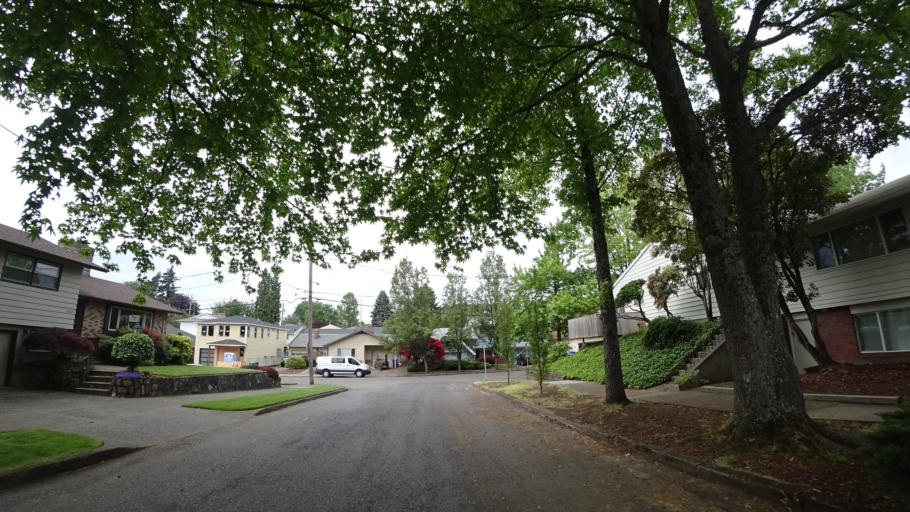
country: US
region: Oregon
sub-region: Clackamas County
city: Milwaukie
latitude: 45.4917
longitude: -122.6278
